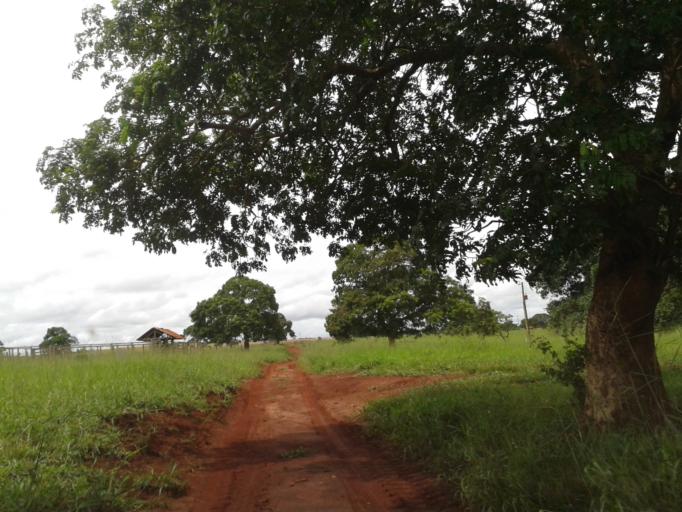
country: BR
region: Minas Gerais
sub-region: Capinopolis
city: Capinopolis
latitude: -18.7811
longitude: -49.7833
